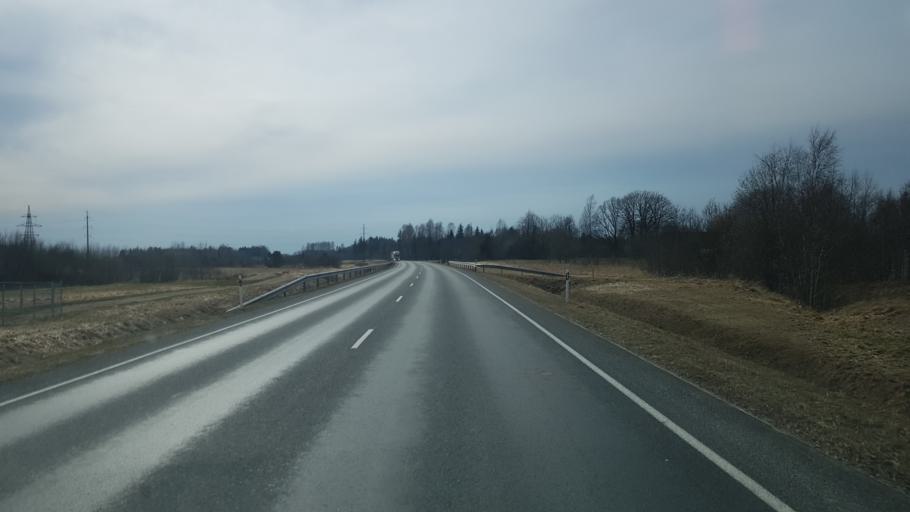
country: EE
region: Paernumaa
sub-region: Vaendra vald (alev)
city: Vandra
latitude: 58.6600
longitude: 25.0137
